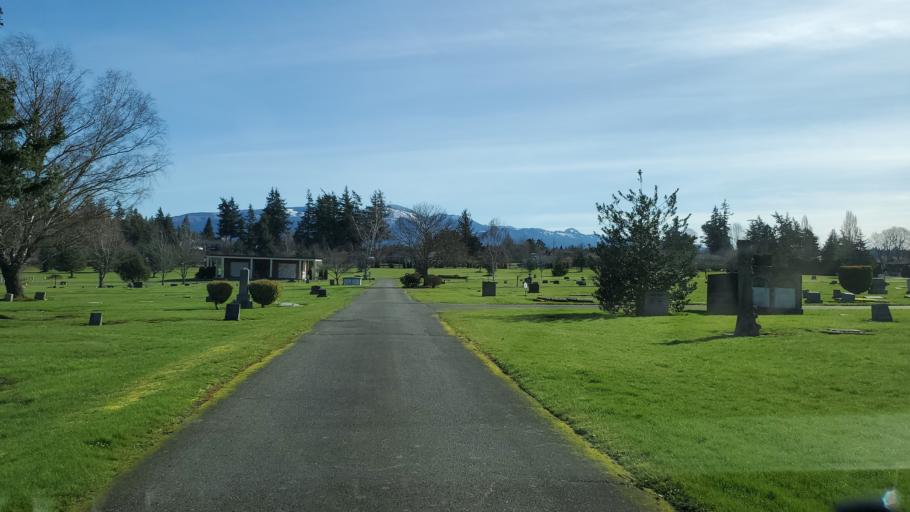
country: US
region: Washington
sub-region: Skagit County
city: Mount Vernon
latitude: 48.4272
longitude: -122.3281
